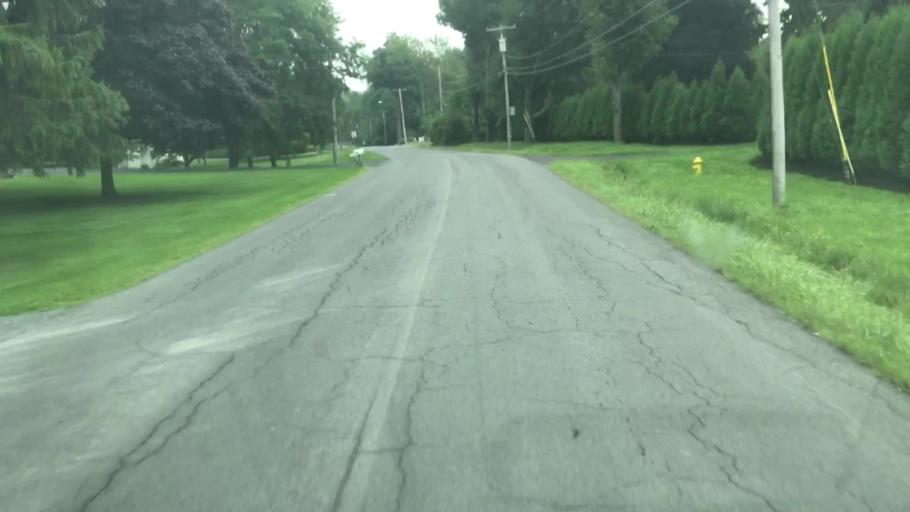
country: US
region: New York
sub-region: Onondaga County
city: Skaneateles
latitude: 42.9551
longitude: -76.4548
